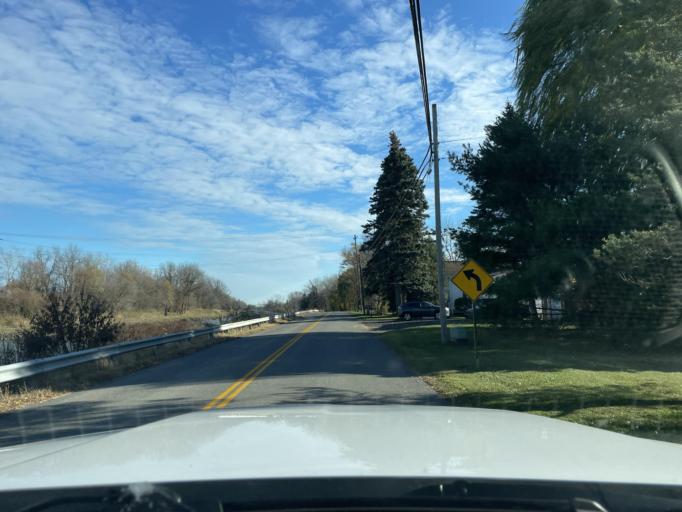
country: US
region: New York
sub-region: Niagara County
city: Gasport
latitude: 43.2019
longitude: -78.5561
